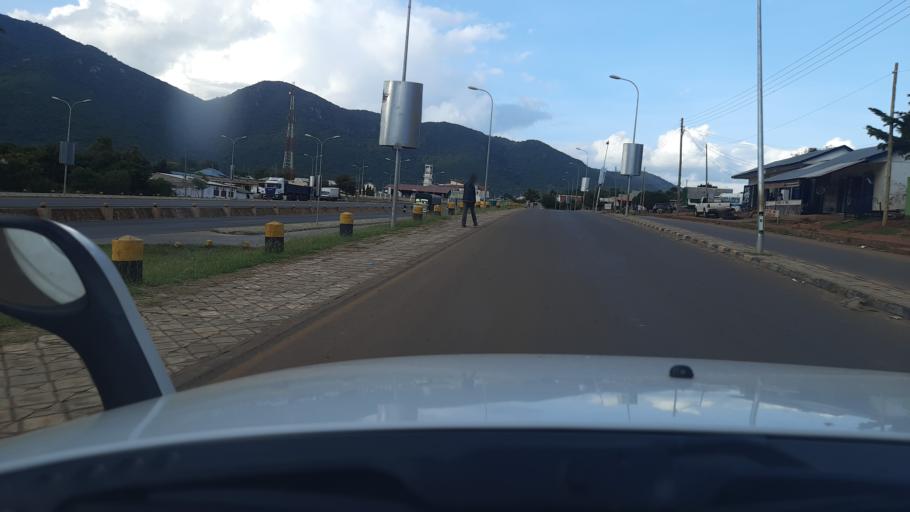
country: TZ
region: Arusha
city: Namanga
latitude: -2.5529
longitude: 36.7836
